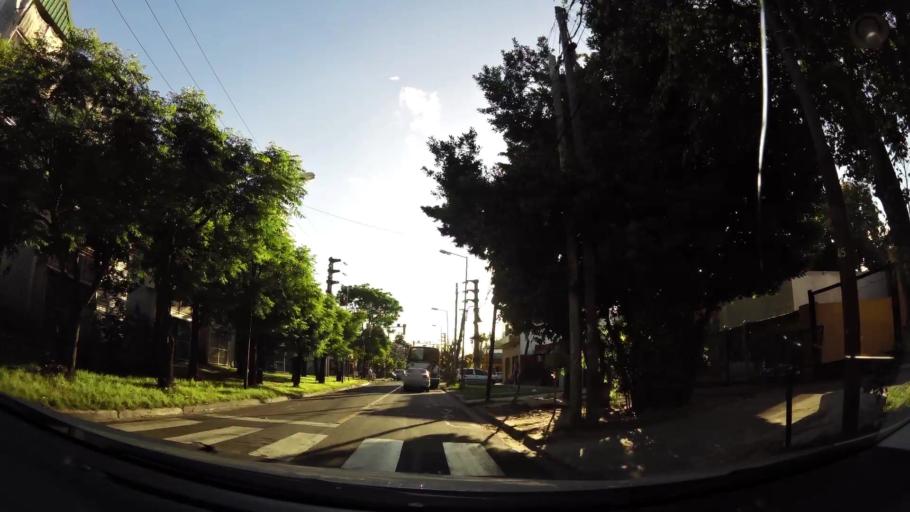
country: AR
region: Buenos Aires
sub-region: Partido de Tigre
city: Tigre
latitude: -34.4617
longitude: -58.5617
